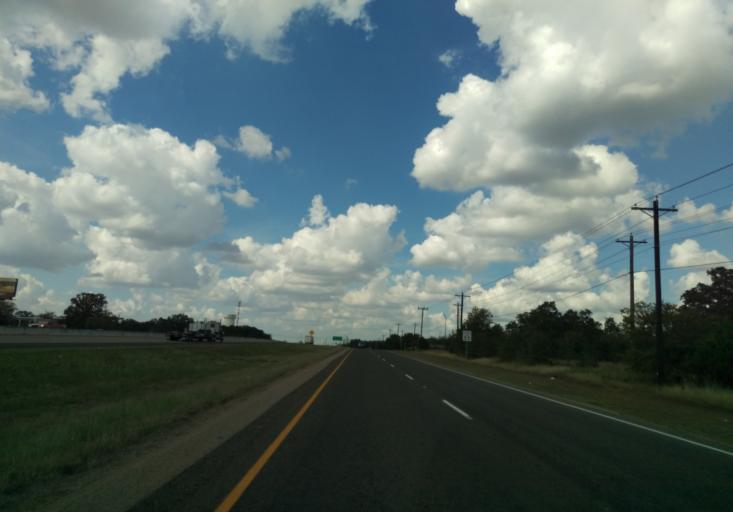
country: US
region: Texas
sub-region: Brazos County
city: College Station
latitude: 30.5505
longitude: -96.2480
